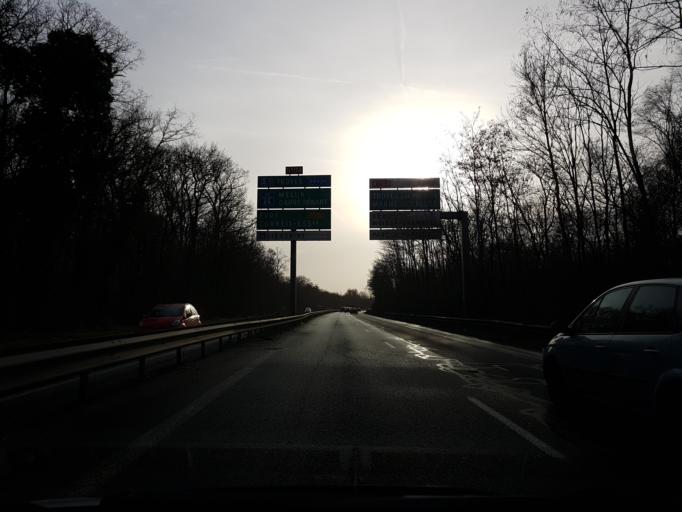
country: FR
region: Ile-de-France
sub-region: Departement de l'Essonne
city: Quincy-sous-Senart
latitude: 48.6502
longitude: 2.5301
